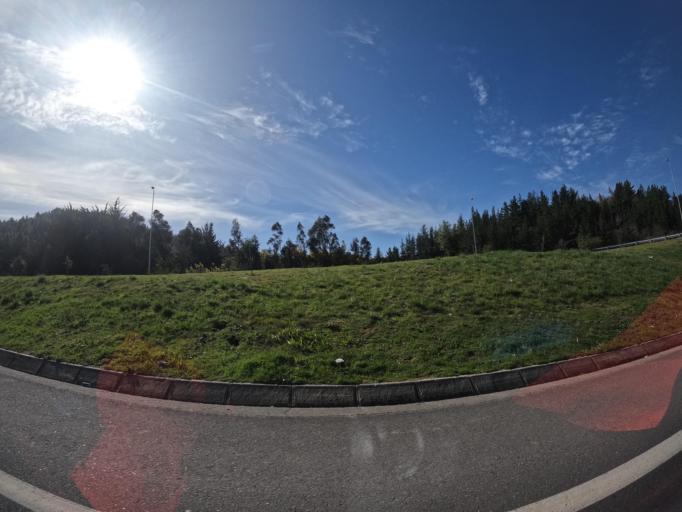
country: CL
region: Biobio
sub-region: Provincia de Biobio
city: Yumbel
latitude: -36.9594
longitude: -72.7326
